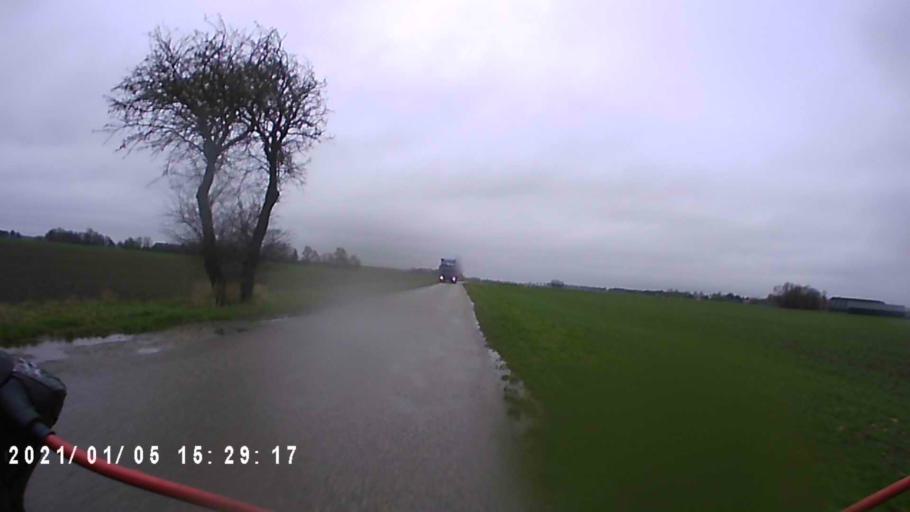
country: DE
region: Lower Saxony
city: Bunde
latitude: 53.2134
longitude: 7.1927
